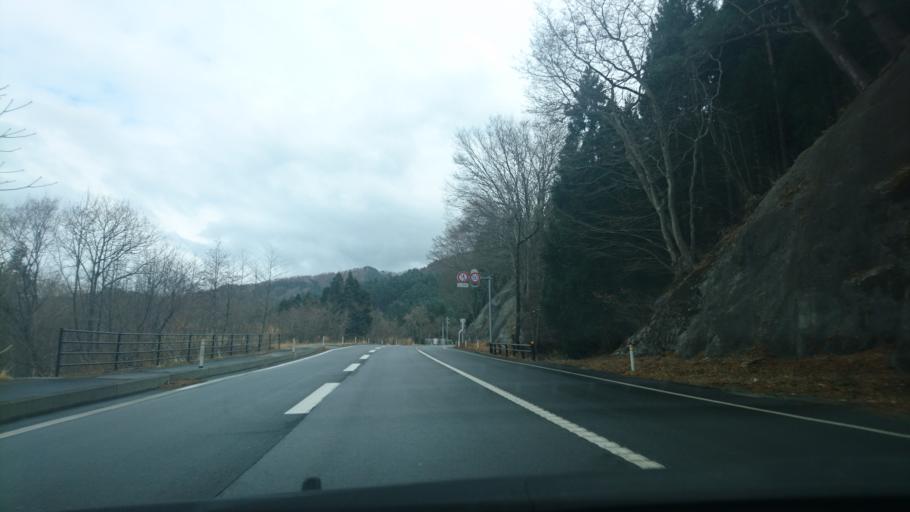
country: JP
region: Iwate
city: Ofunato
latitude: 39.1358
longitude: 141.8214
